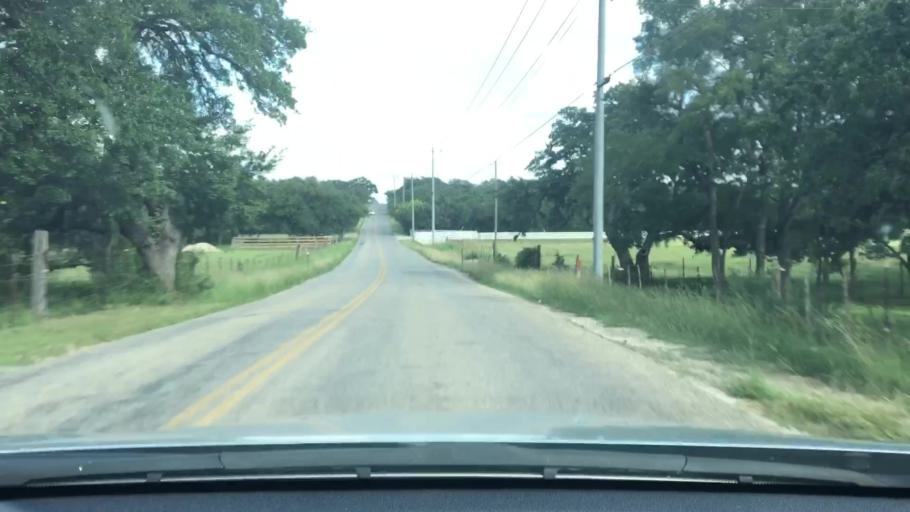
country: US
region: Texas
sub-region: Bexar County
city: Fair Oaks Ranch
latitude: 29.7853
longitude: -98.6336
